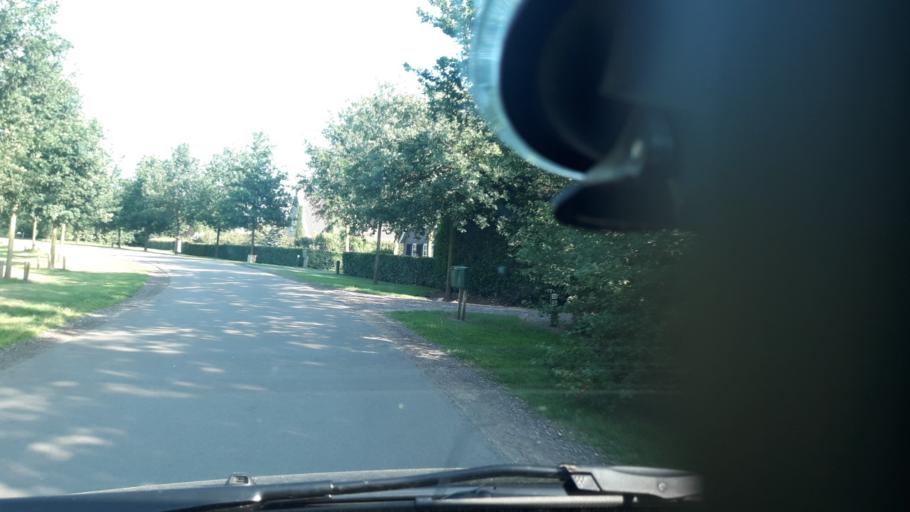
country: NL
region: Gelderland
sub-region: Gemeente Ermelo
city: Horst
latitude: 52.3207
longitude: 5.5796
